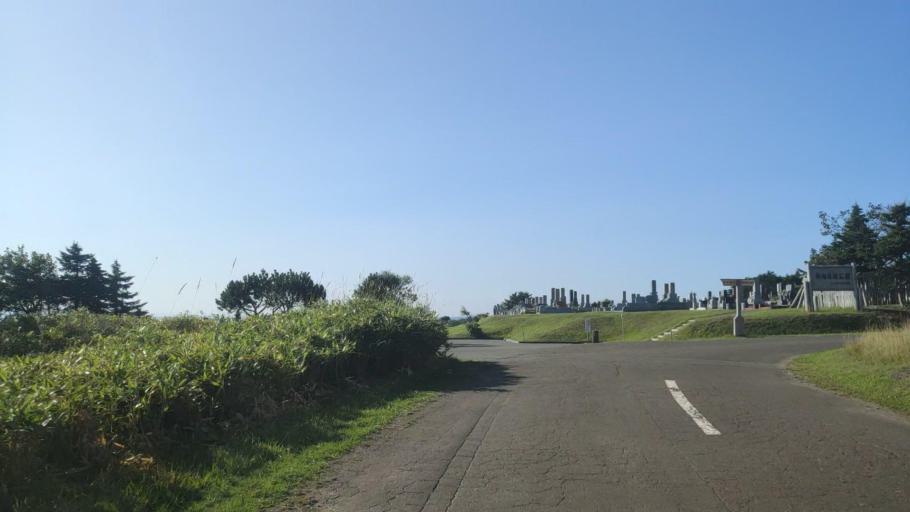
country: JP
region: Hokkaido
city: Wakkanai
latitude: 45.4166
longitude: 141.6687
